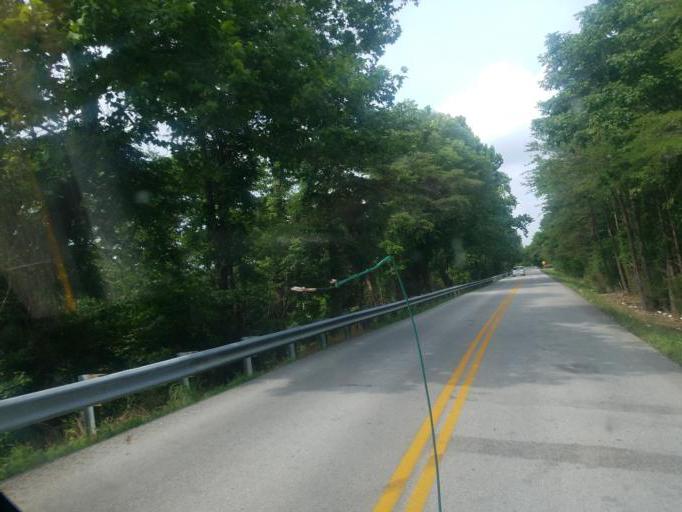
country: US
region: Kentucky
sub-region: Edmonson County
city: Brownsville
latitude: 37.3415
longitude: -86.1281
